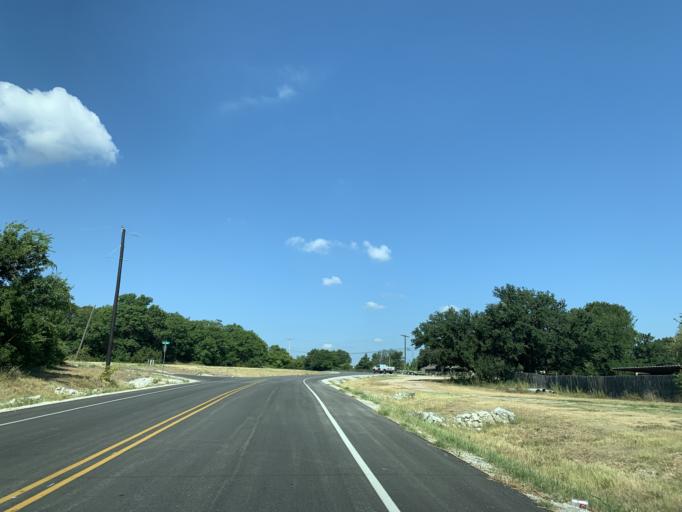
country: US
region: Texas
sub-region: Tarrant County
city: Azle
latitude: 32.8593
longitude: -97.5220
